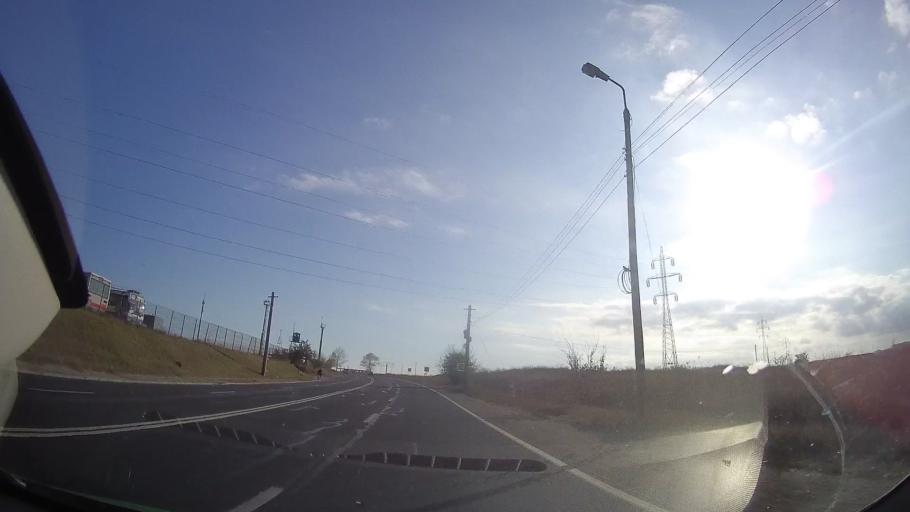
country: RO
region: Constanta
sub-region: Municipiul Mangalia
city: Mangalia
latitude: 43.7990
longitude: 28.5592
